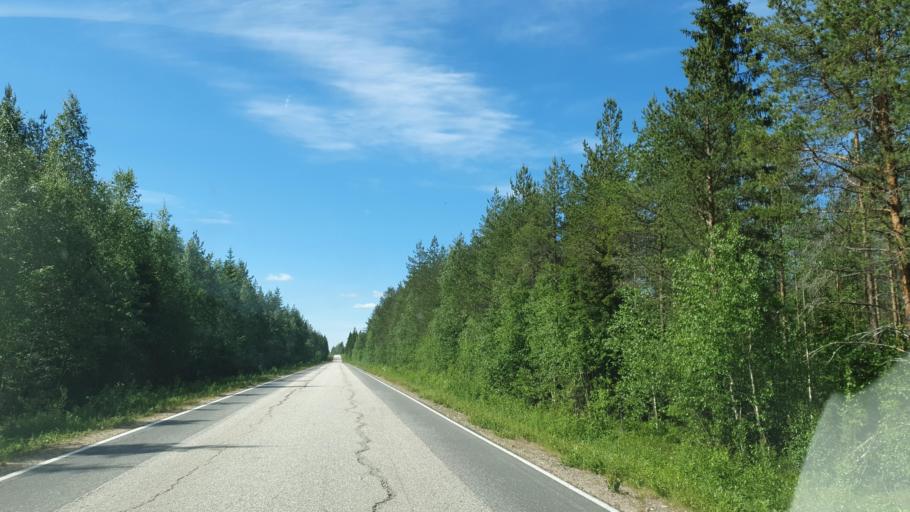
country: FI
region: Kainuu
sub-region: Kehys-Kainuu
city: Suomussalmi
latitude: 64.5916
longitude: 29.0818
